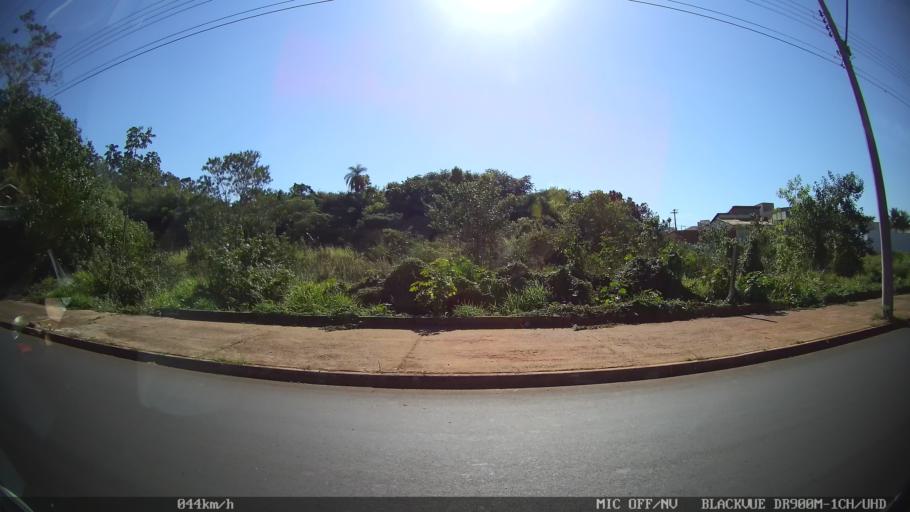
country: BR
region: Sao Paulo
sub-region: Batatais
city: Batatais
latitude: -20.8819
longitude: -47.5898
